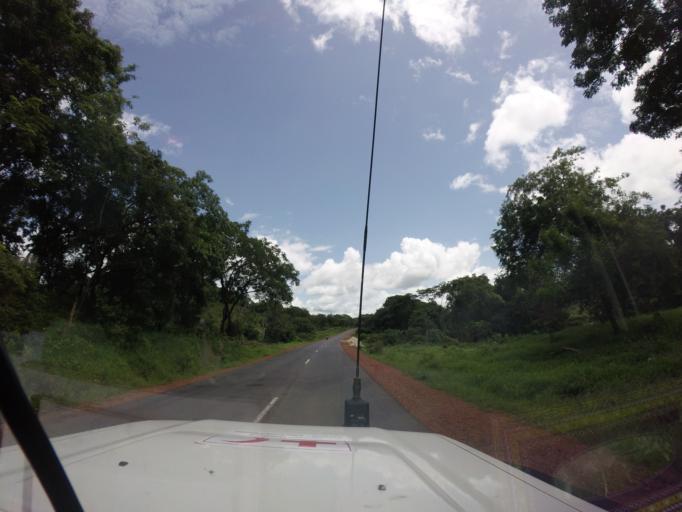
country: SL
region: Northern Province
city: Gberia Fotombu
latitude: 10.1643
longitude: -11.2510
